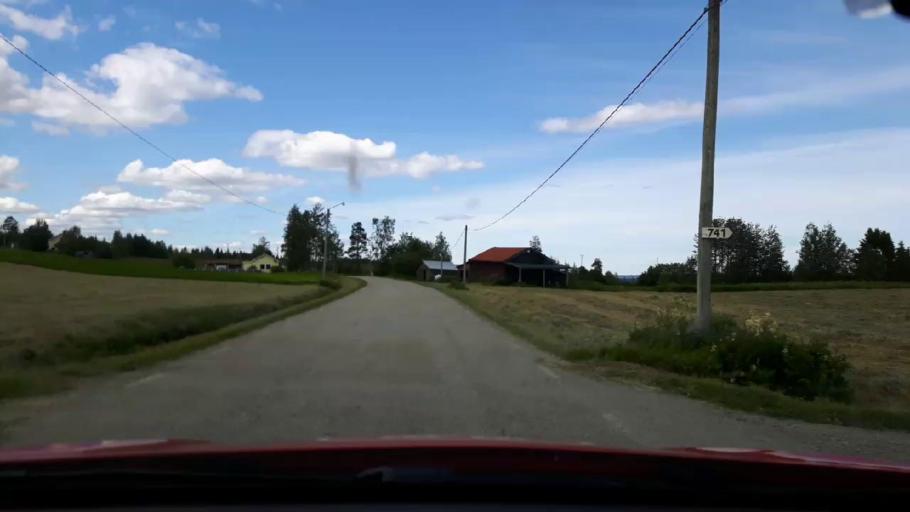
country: SE
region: Jaemtland
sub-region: Bergs Kommun
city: Hoverberg
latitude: 62.8309
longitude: 14.4581
